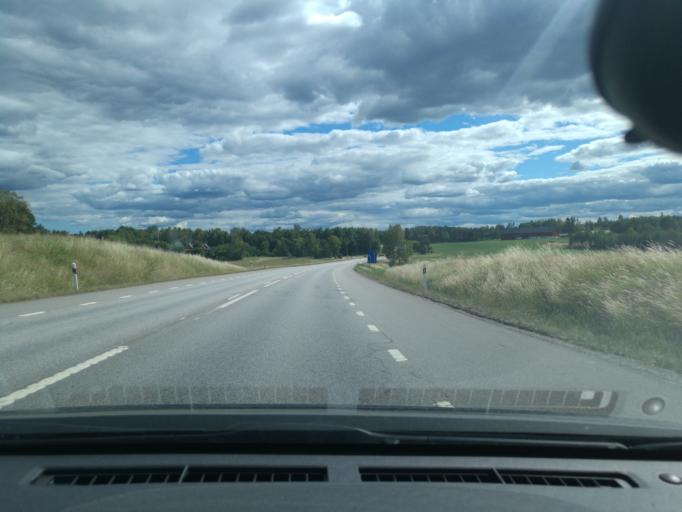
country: SE
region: OEstergoetland
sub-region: Soderkopings Kommun
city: Soederkoeping
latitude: 58.4564
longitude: 16.3659
